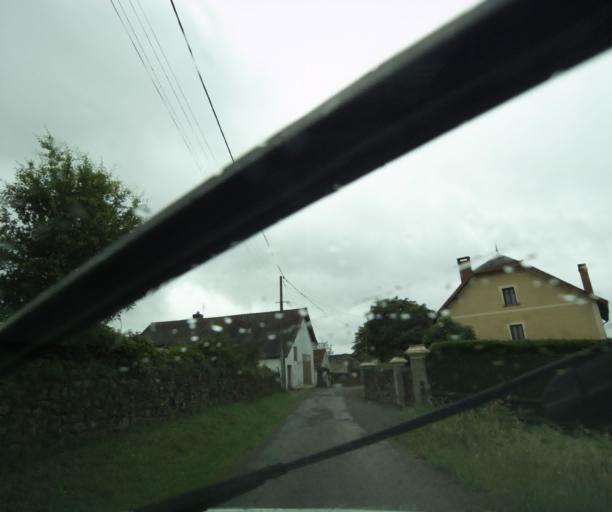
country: FR
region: Bourgogne
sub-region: Departement de Saone-et-Loire
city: Charolles
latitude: 46.4940
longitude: 4.3556
